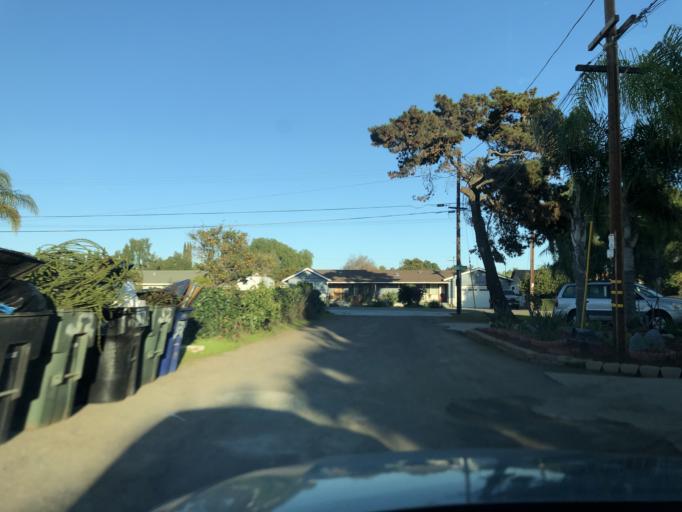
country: US
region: California
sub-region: San Diego County
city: Chula Vista
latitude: 32.6528
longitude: -117.0599
